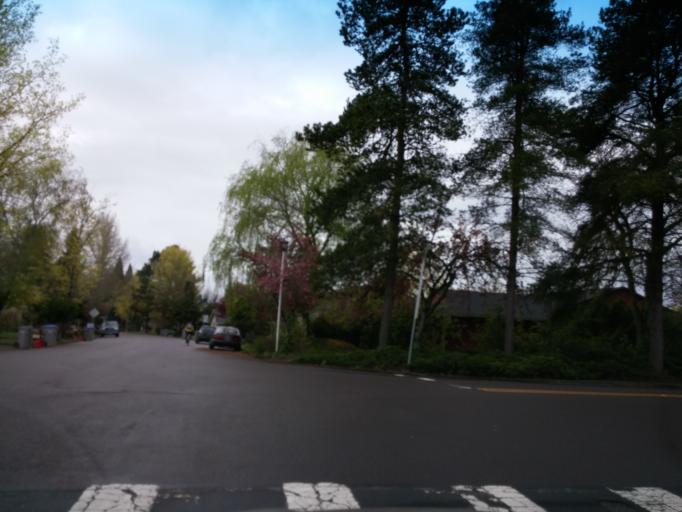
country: US
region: Oregon
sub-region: Washington County
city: Oak Hills
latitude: 45.5386
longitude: -122.8398
